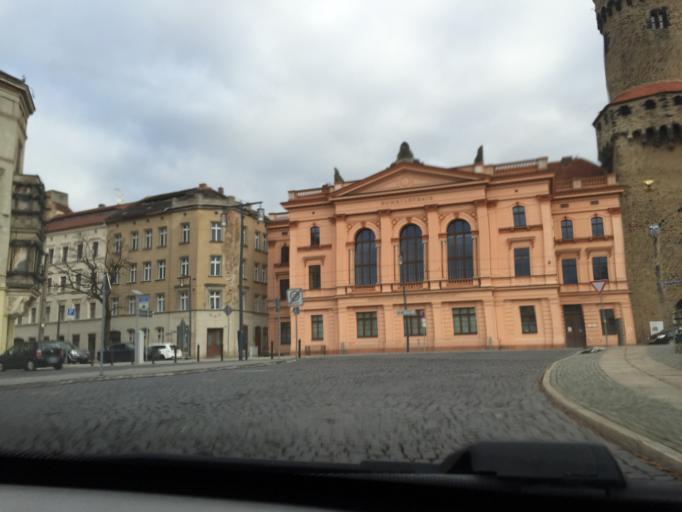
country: DE
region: Saxony
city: Goerlitz
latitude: 51.1548
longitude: 14.9845
